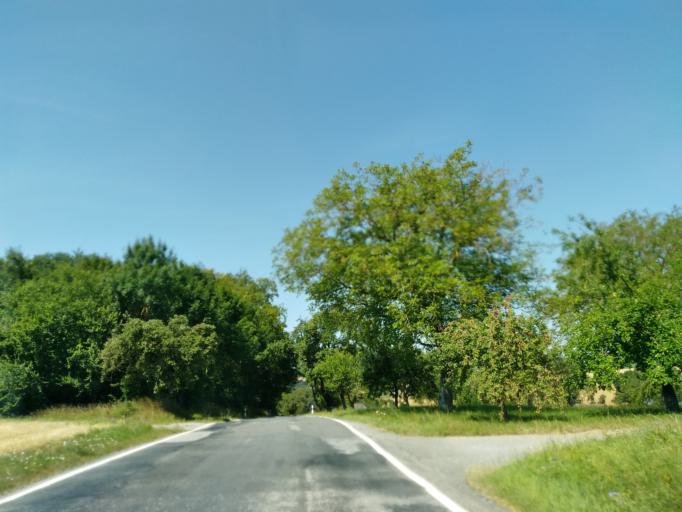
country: DE
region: Baden-Wuerttemberg
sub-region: Karlsruhe Region
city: Billigheim
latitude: 49.3898
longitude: 9.2828
